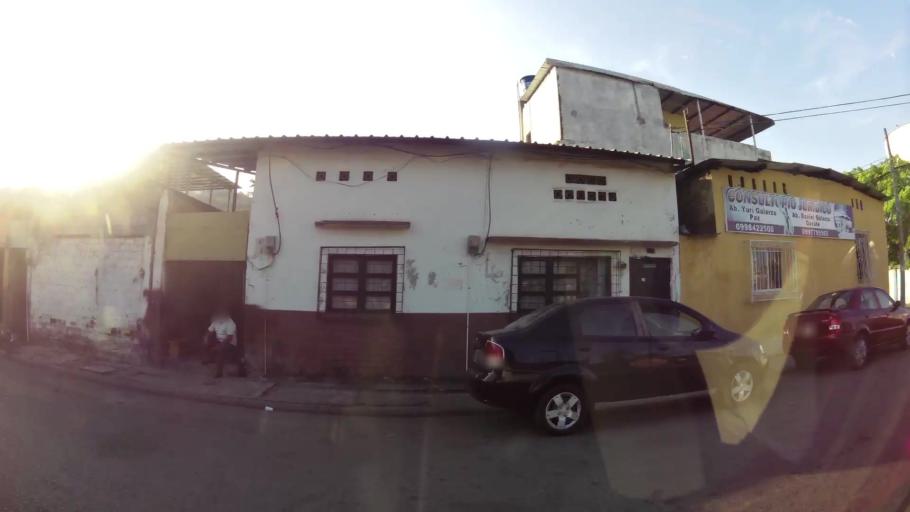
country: EC
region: Guayas
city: Eloy Alfaro
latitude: -2.1733
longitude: -79.8543
